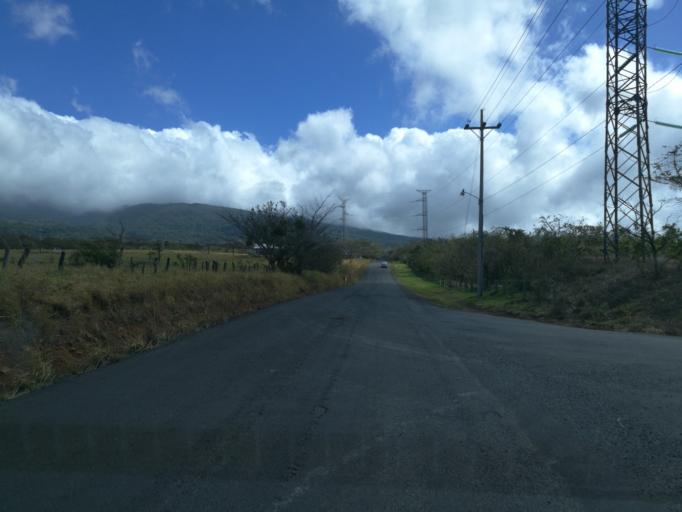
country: CR
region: Guanacaste
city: Liberia
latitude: 10.7578
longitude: -85.3623
